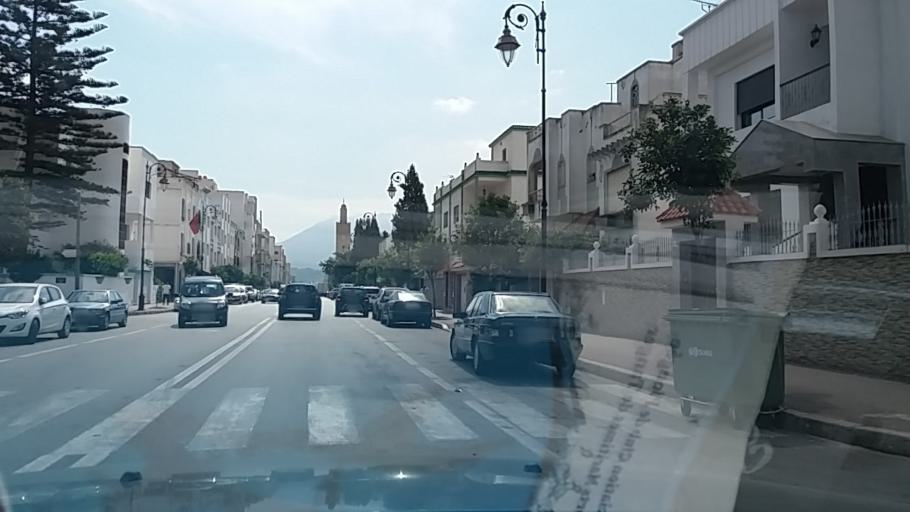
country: MA
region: Tanger-Tetouan
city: Tetouan
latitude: 35.5837
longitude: -5.3459
